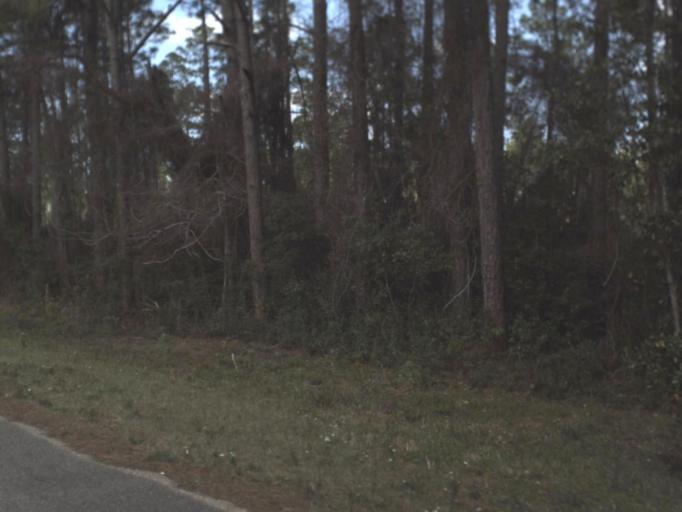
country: US
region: Florida
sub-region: Gulf County
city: Port Saint Joe
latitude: 29.7359
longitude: -85.1600
